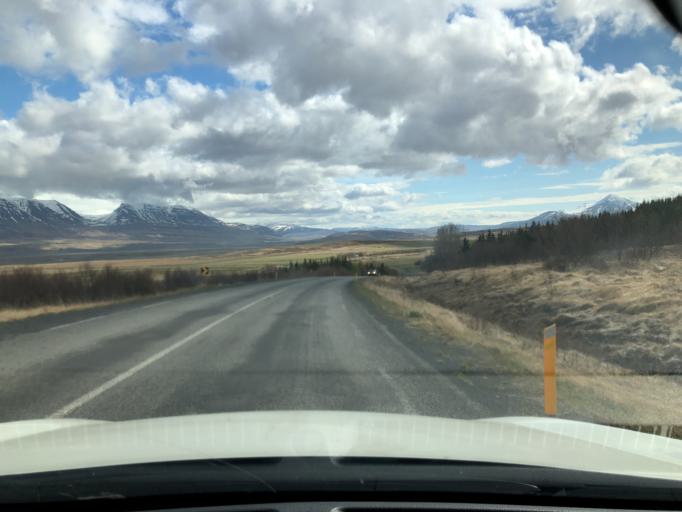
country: IS
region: Northwest
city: Saudarkrokur
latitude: 65.5486
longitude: -19.4786
